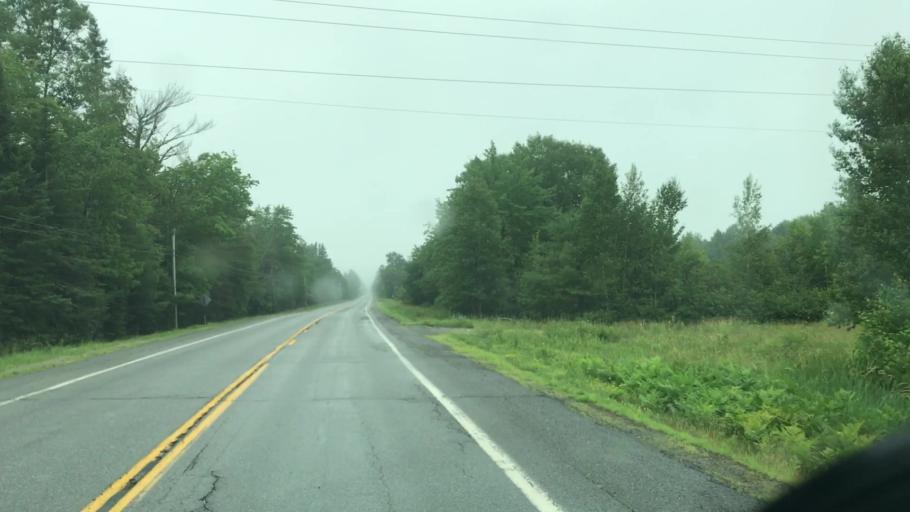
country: US
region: Maine
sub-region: Penobscot County
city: Howland
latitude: 45.2511
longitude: -68.6381
